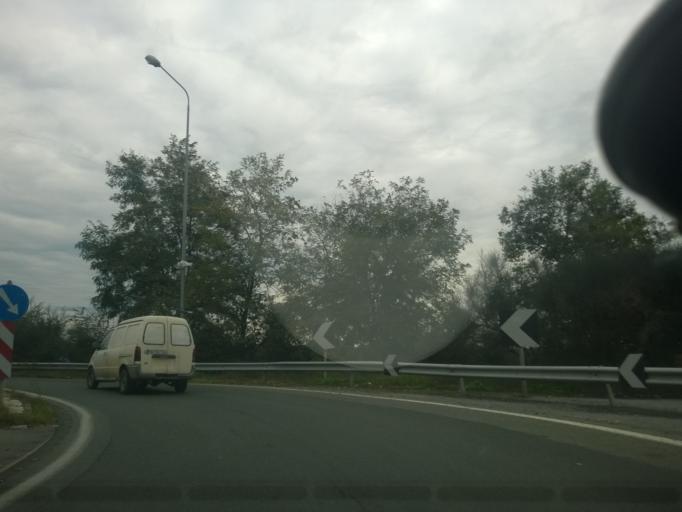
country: GR
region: Central Macedonia
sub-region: Nomos Pellis
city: Mavrovouni
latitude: 40.7876
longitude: 22.1619
